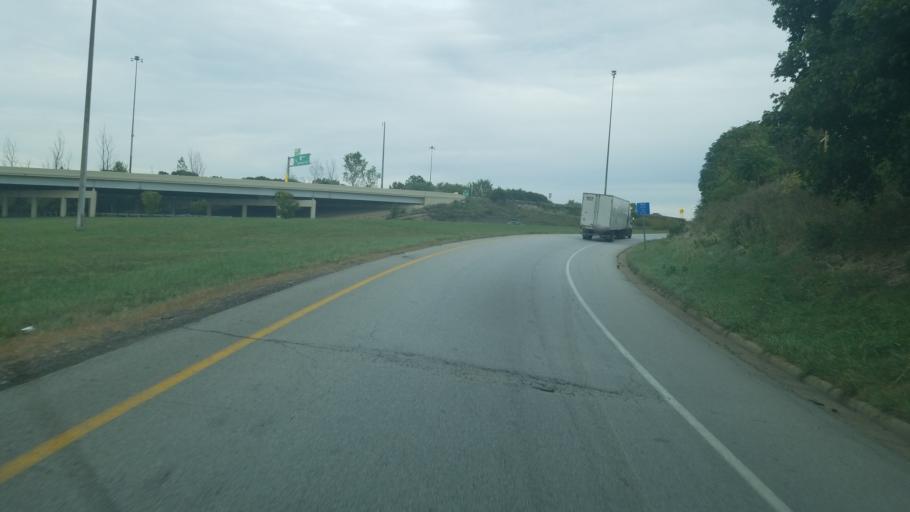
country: US
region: Ohio
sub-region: Summit County
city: Akron
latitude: 41.0615
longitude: -81.5002
